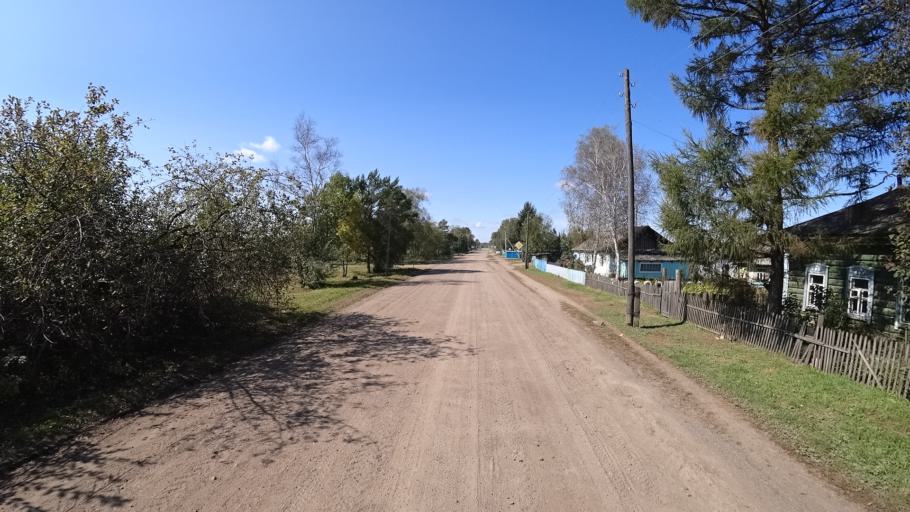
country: RU
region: Amur
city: Arkhara
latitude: 49.4022
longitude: 130.1454
